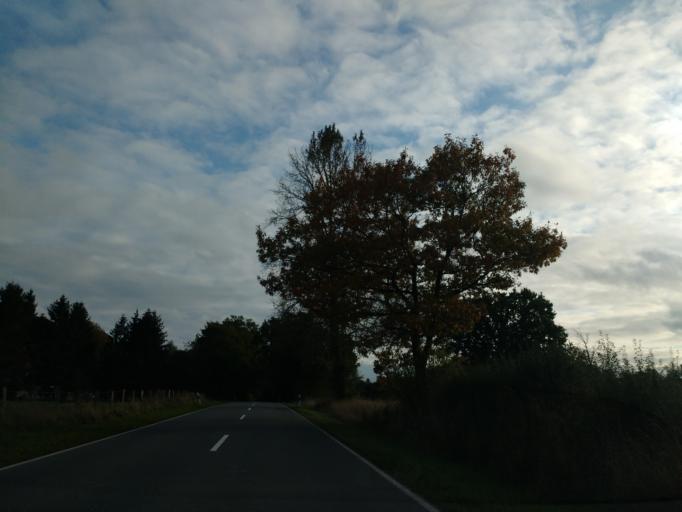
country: DE
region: Schleswig-Holstein
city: Schonwalde am Bungsberg
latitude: 54.2107
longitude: 10.7395
